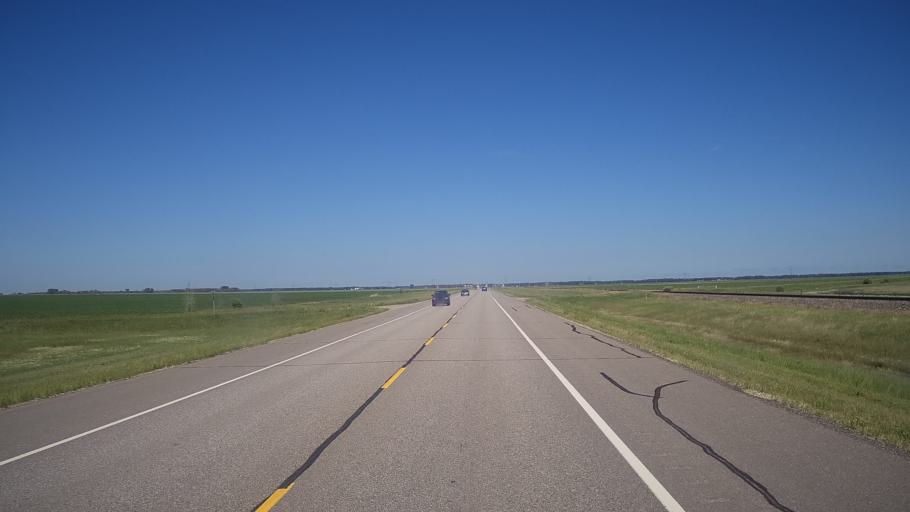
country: CA
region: Manitoba
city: Portage la Prairie
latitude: 50.1025
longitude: -98.5363
